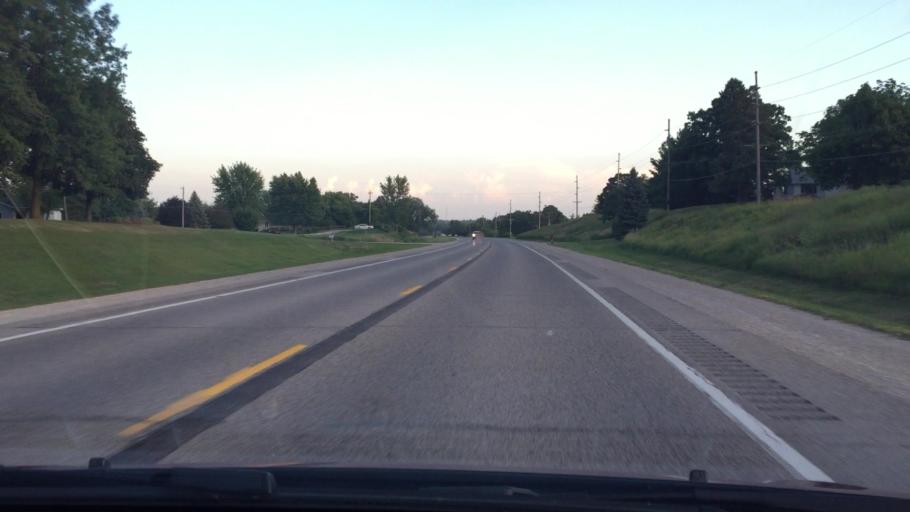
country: US
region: Iowa
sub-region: Muscatine County
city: Muscatine
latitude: 41.4737
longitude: -91.0378
